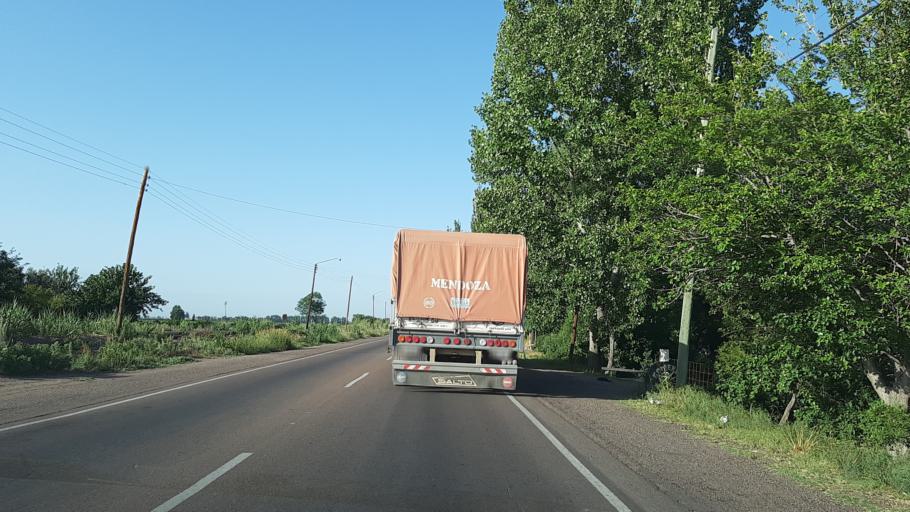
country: AR
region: Mendoza
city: San Martin
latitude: -32.9900
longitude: -68.4689
